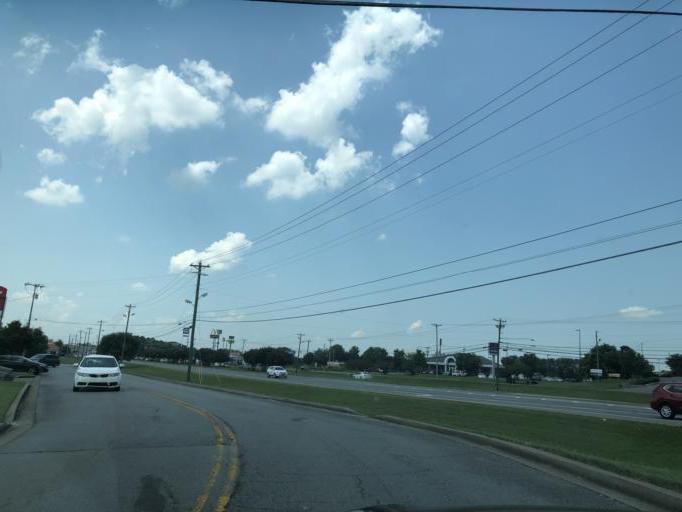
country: US
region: Tennessee
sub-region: Rutherford County
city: Murfreesboro
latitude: 35.8461
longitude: -86.4265
